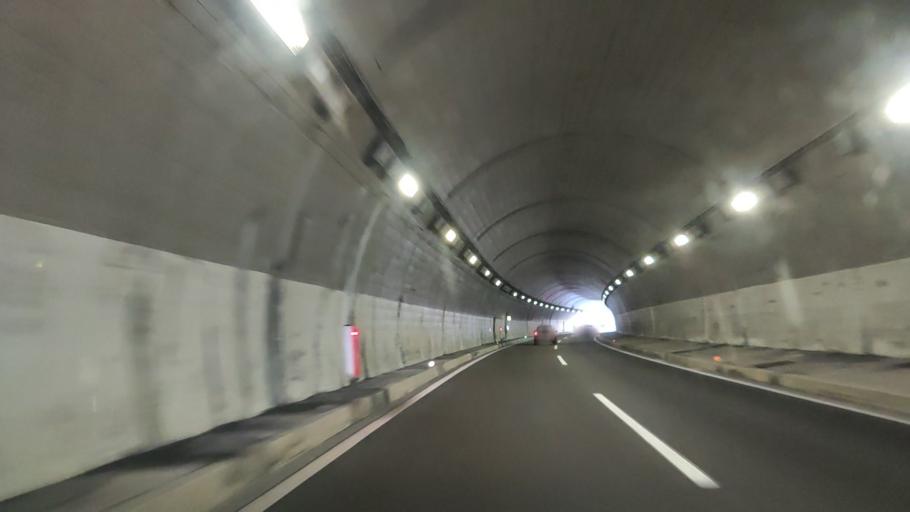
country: JP
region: Ehime
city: Kawanoecho
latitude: 33.9653
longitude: 133.5400
